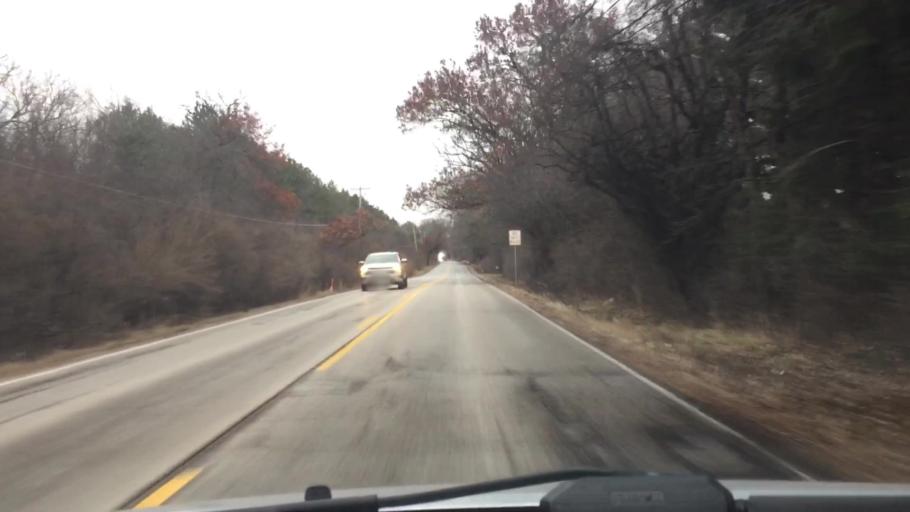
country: US
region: Wisconsin
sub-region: Waukesha County
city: Delafield
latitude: 43.0366
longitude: -88.4043
